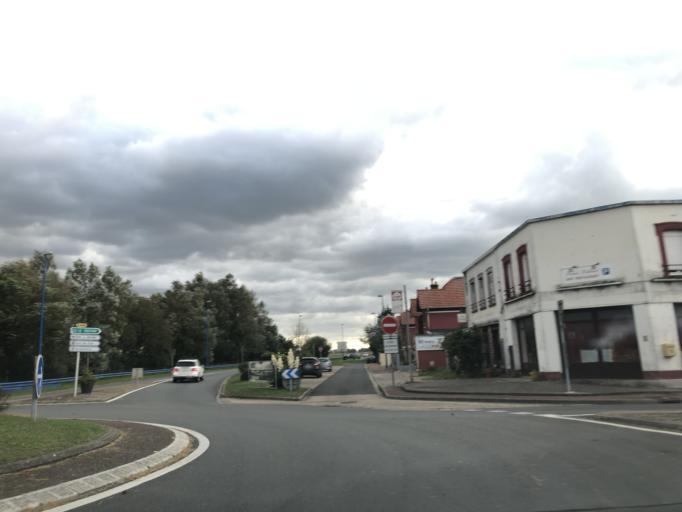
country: FR
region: Picardie
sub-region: Departement de la Somme
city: Ault
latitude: 50.0949
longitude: 1.4633
